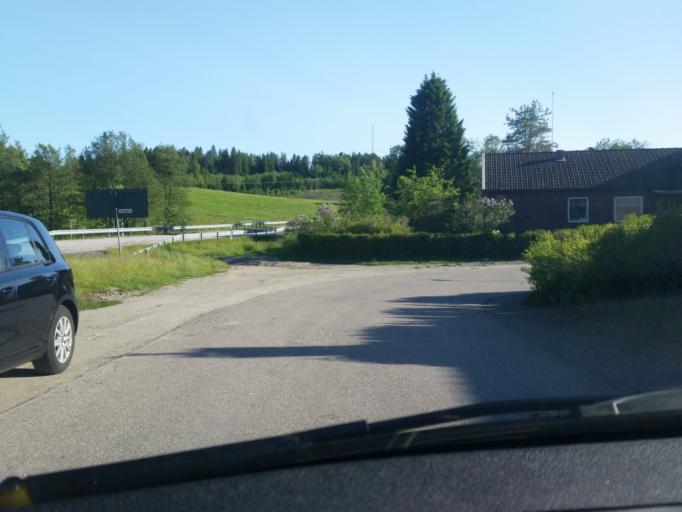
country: SE
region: Vaestra Goetaland
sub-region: Fargelanda Kommun
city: Faergelanda
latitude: 58.5676
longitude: 12.0036
